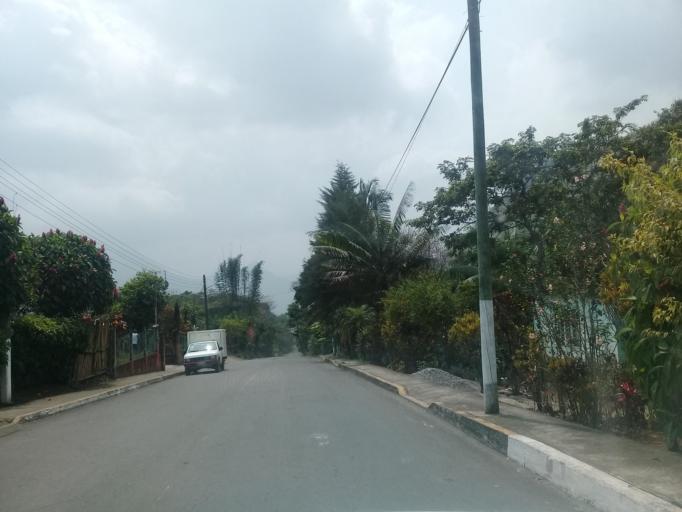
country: MX
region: Veracruz
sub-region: Cordoba
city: Fredepo
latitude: 18.8575
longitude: -96.9914
